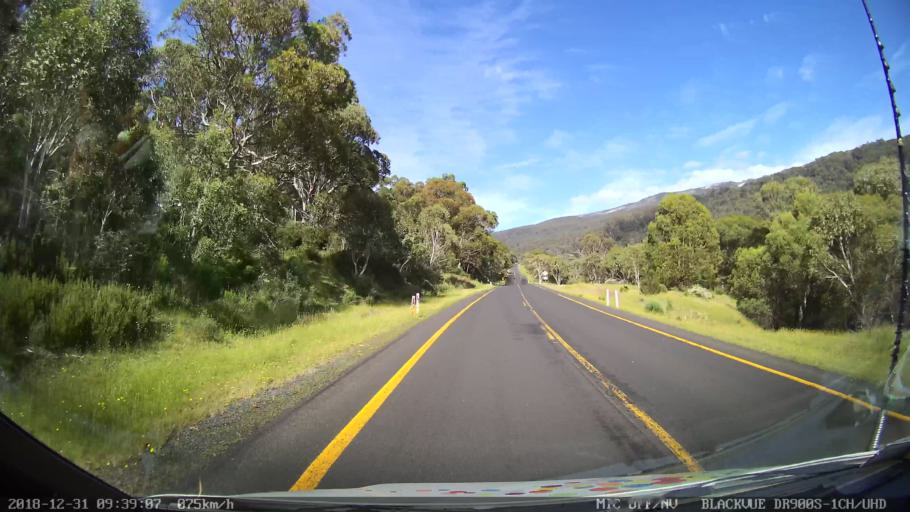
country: AU
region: New South Wales
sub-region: Snowy River
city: Jindabyne
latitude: -36.4781
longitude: 148.3594
